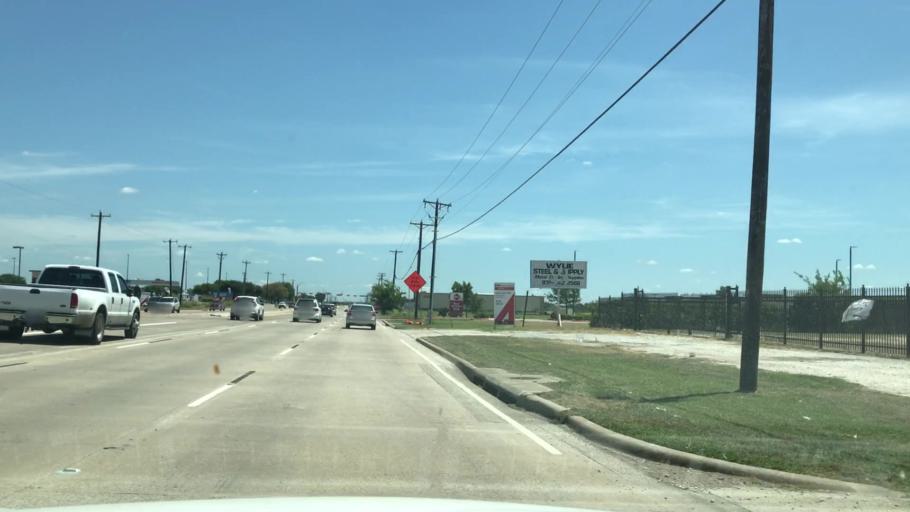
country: US
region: Texas
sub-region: Collin County
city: Wylie
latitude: 33.0228
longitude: -96.5148
